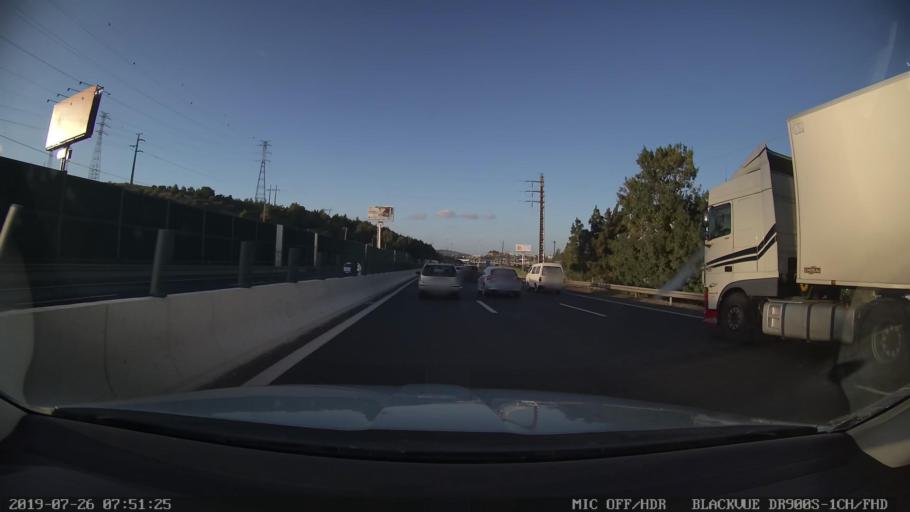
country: PT
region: Lisbon
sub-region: Vila Franca de Xira
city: Vialonga
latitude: 38.8836
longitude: -9.0606
